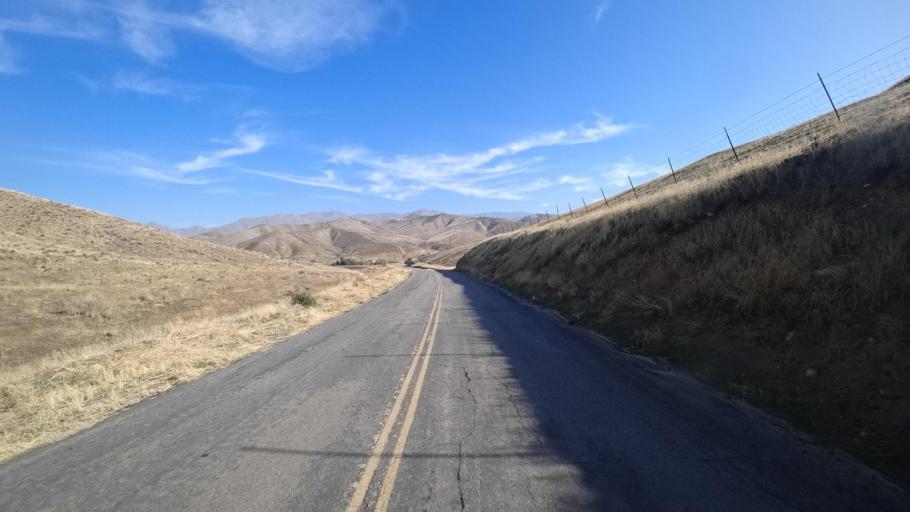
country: US
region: California
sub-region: Kern County
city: Lamont
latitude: 35.3964
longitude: -118.8149
